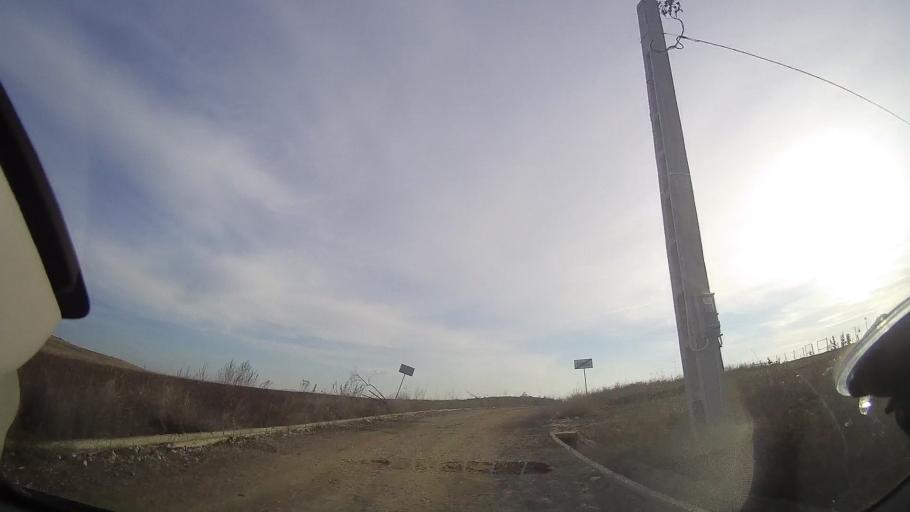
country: RO
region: Bihor
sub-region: Comuna Tileagd
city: Tileagd
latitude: 47.0996
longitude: 22.1765
